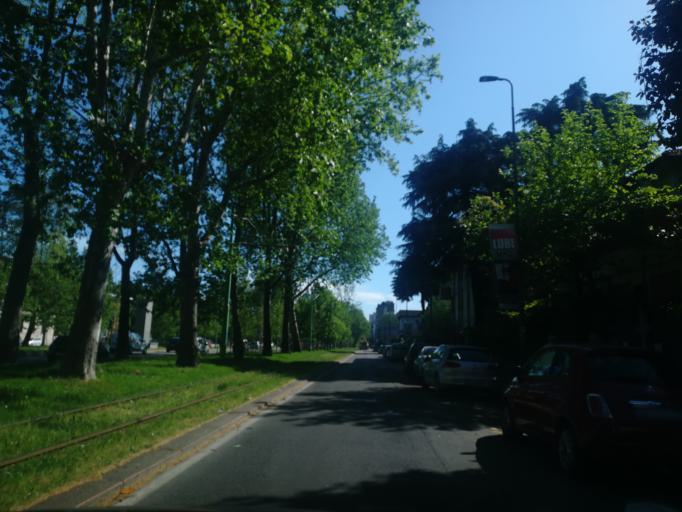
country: IT
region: Lombardy
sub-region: Citta metropolitana di Milano
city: Milano
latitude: 45.4977
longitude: 9.1954
